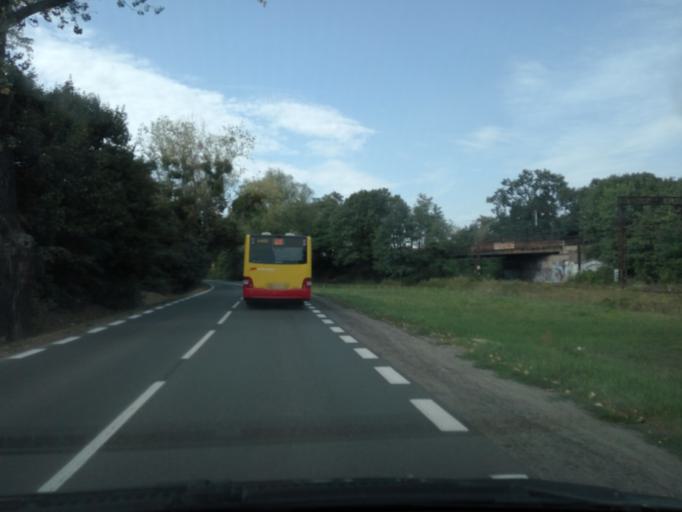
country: PL
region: Lower Silesian Voivodeship
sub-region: Powiat wroclawski
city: Radwanice
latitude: 51.0729
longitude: 17.0778
